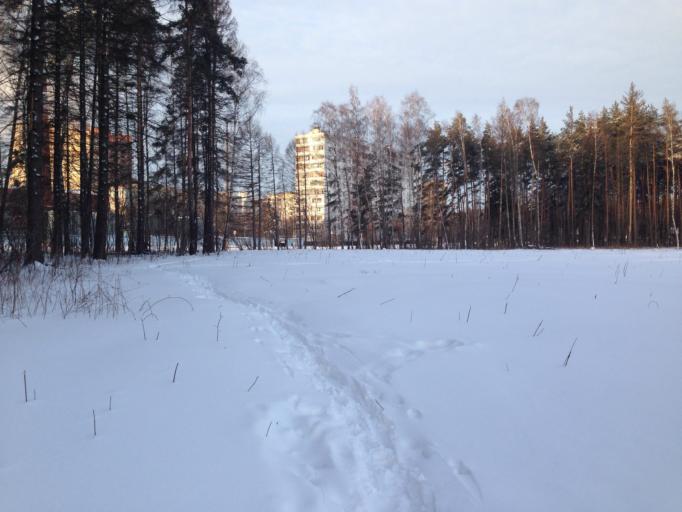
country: RU
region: Moskovskaya
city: Balashikha
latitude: 55.8164
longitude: 37.9737
